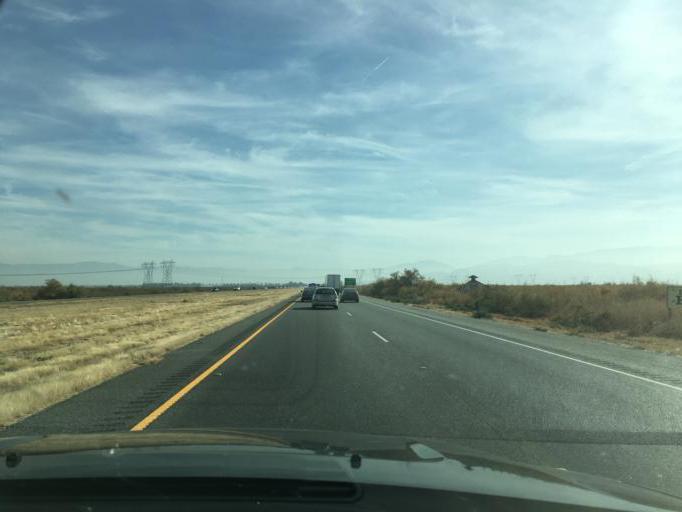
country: US
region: California
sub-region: Kern County
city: Greenfield
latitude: 35.1097
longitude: -119.0536
